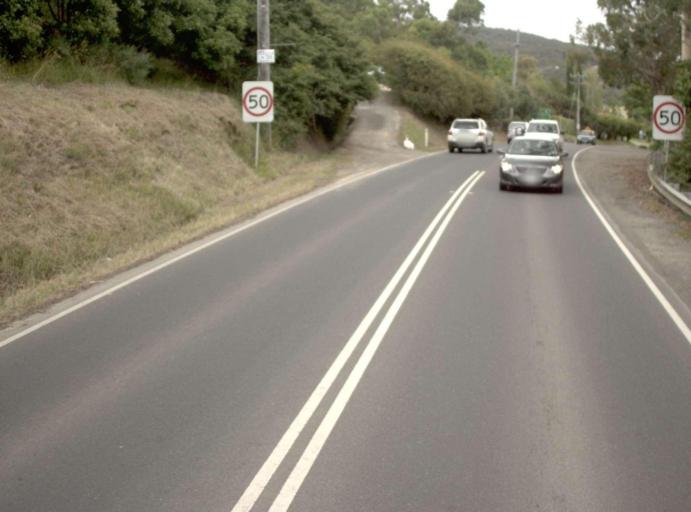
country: AU
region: Victoria
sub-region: Yarra Ranges
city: Yarra Junction
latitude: -37.7816
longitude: 145.6176
